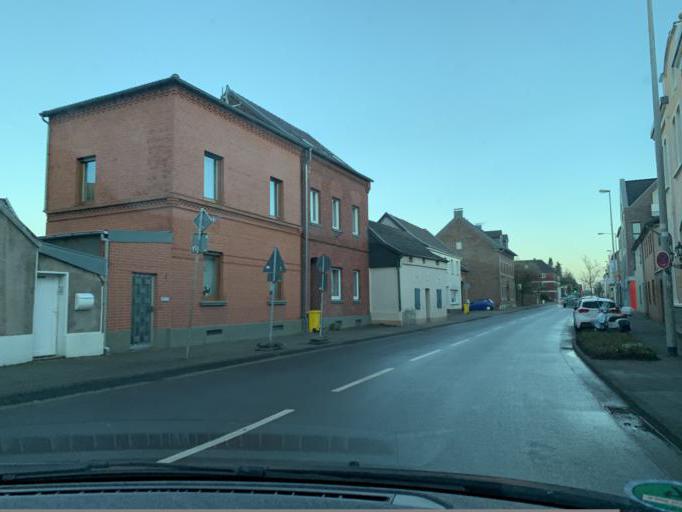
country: DE
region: North Rhine-Westphalia
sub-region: Regierungsbezirk Dusseldorf
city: Juchen
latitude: 51.1012
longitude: 6.5049
